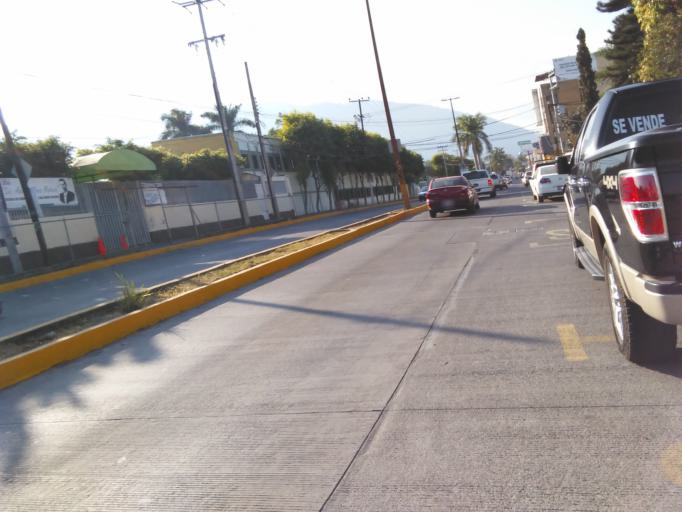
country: MX
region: Nayarit
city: Tepic
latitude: 21.4993
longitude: -104.8984
